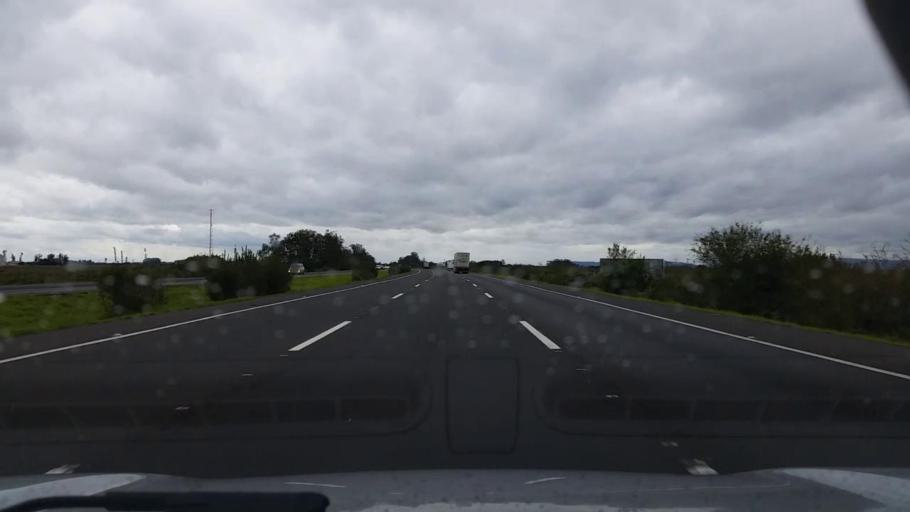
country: BR
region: Rio Grande do Sul
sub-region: Rolante
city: Rolante
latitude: -29.8863
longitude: -50.6609
